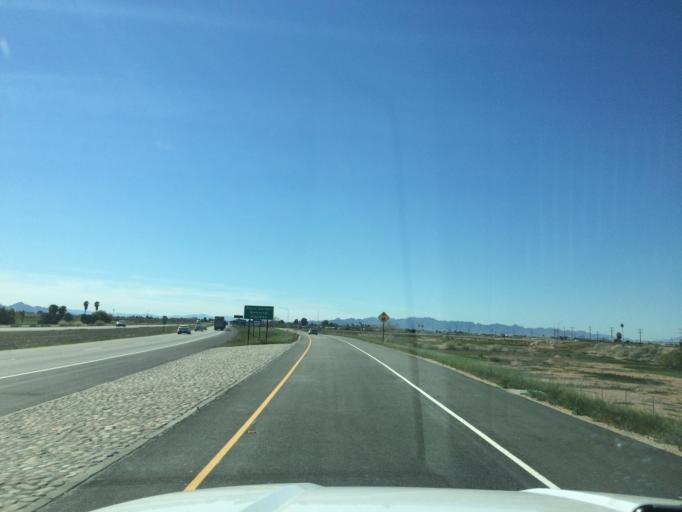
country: US
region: Arizona
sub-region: La Paz County
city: Ehrenberg
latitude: 33.6081
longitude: -114.5448
